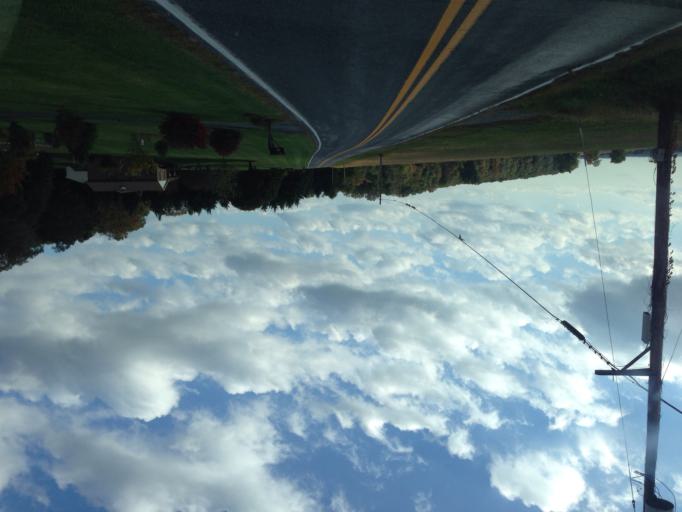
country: US
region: Maryland
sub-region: Carroll County
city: Mount Airy
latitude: 39.3338
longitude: -77.1445
